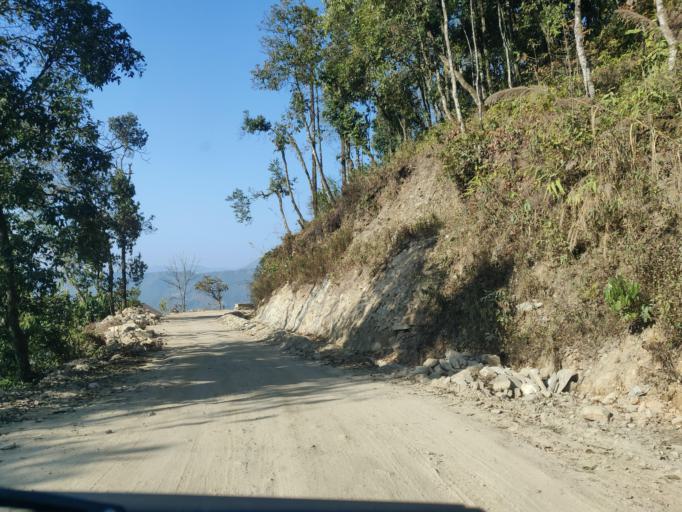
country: NP
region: Western Region
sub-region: Gandaki Zone
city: Pokhara
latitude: 28.2390
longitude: 83.9624
